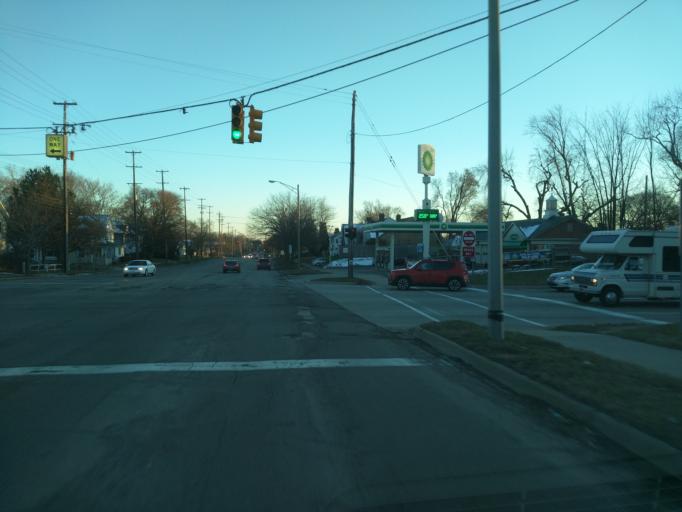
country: US
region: Michigan
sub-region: Ingham County
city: Lansing
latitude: 42.7253
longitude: -84.5382
